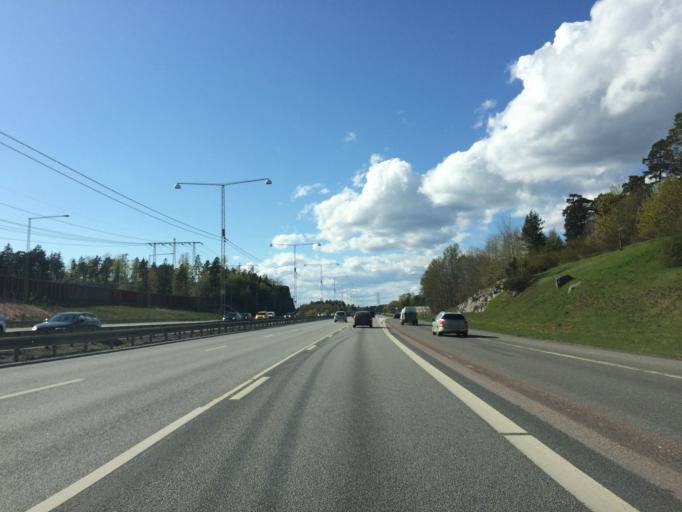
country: SE
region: Stockholm
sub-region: Stockholms Kommun
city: Kista
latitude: 59.4136
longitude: 17.9436
